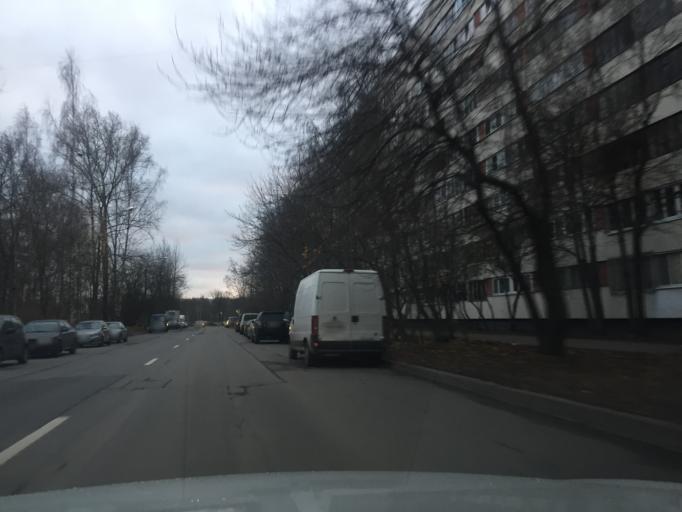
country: RU
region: St.-Petersburg
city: Grazhdanka
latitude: 60.0236
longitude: 30.4276
